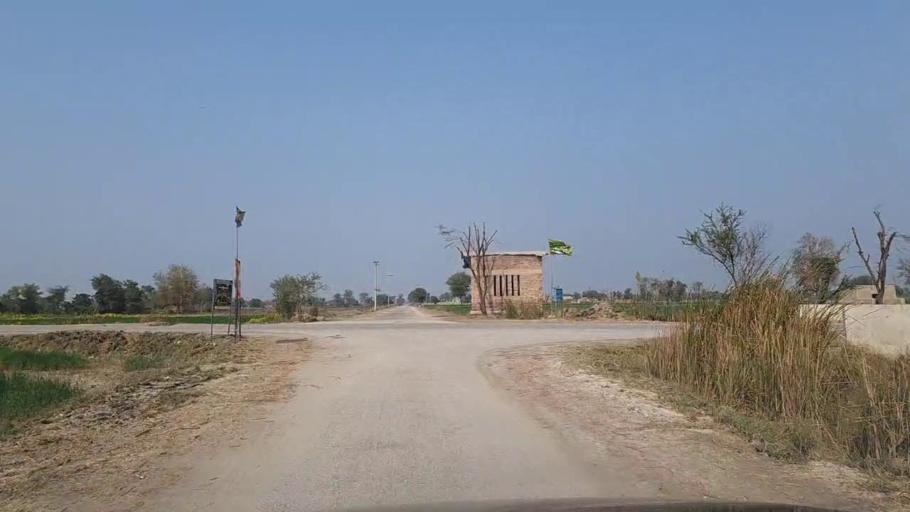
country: PK
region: Sindh
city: Daur
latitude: 26.4042
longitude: 68.4240
